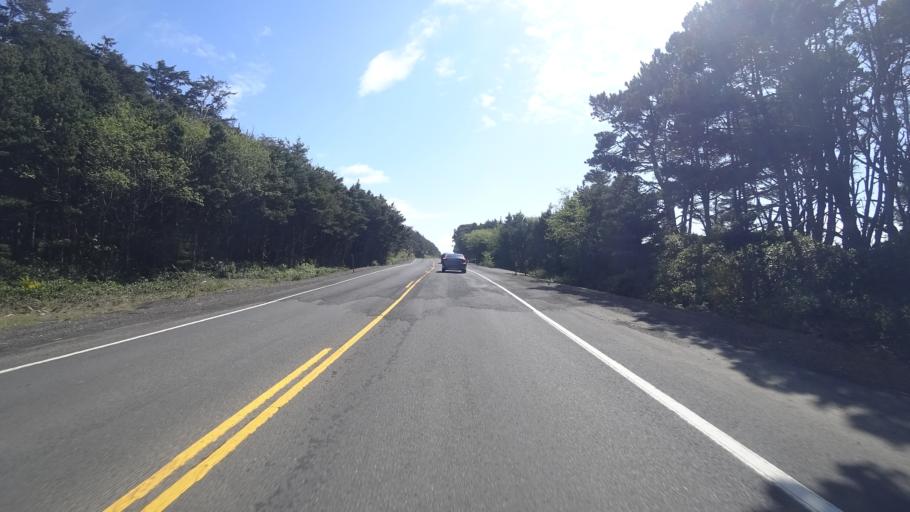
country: US
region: Oregon
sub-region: Lincoln County
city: Newport
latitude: 44.6968
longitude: -124.0623
